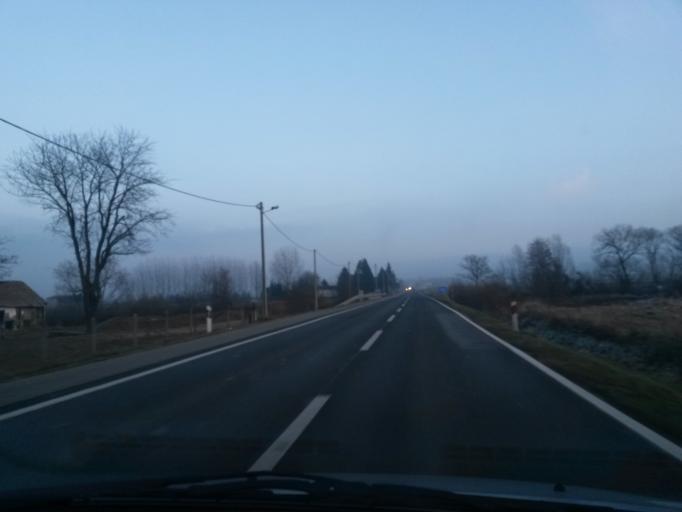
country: HR
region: Koprivnicko-Krizevacka
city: Reka
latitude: 46.1963
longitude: 16.7229
